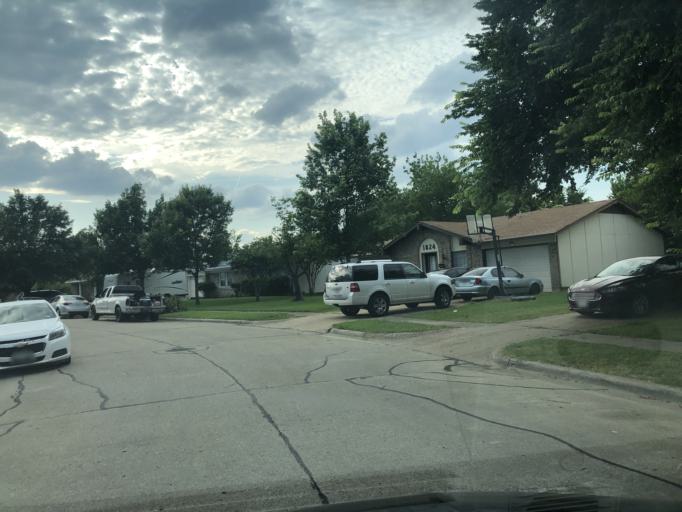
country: US
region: Texas
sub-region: Dallas County
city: Irving
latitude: 32.7917
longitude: -96.9708
